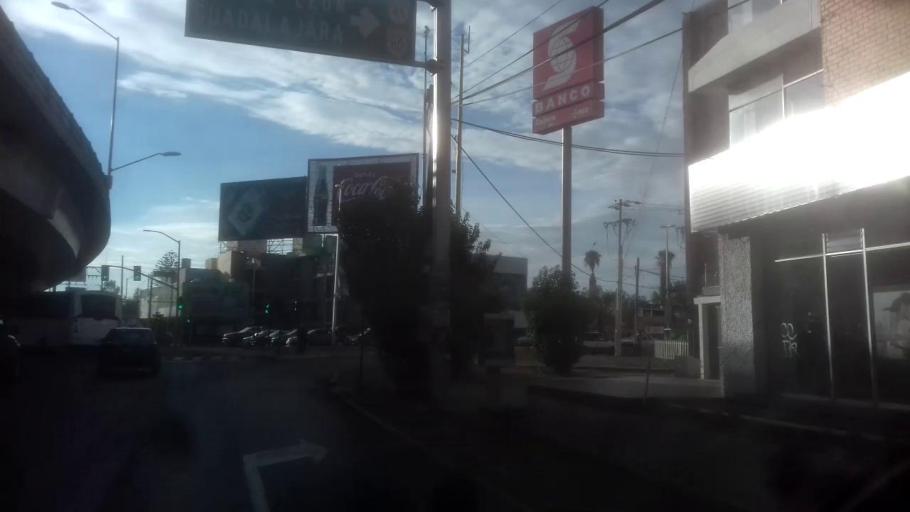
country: MX
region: Aguascalientes
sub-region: Aguascalientes
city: Aguascalientes
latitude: 21.8653
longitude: -102.2946
